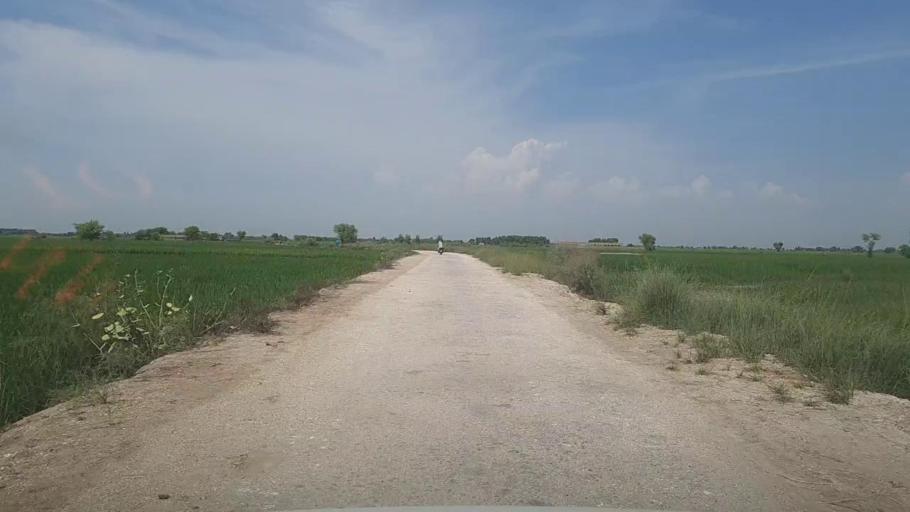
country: PK
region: Sindh
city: Kandhkot
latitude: 28.2837
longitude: 69.2378
